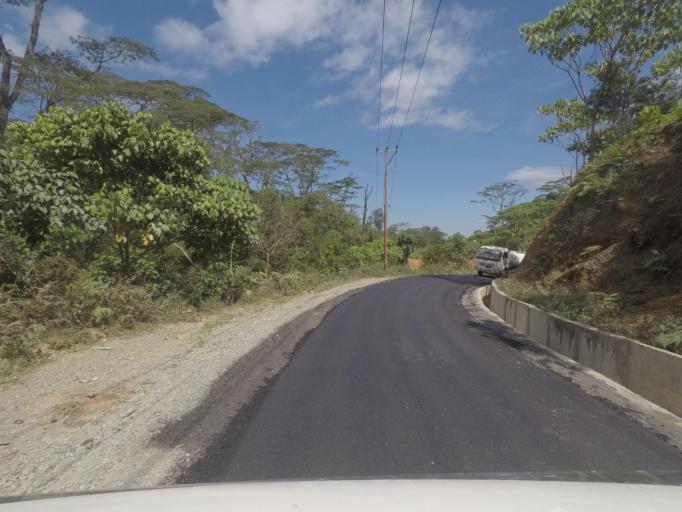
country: TL
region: Ermera
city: Gleno
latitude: -8.7500
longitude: 125.3408
